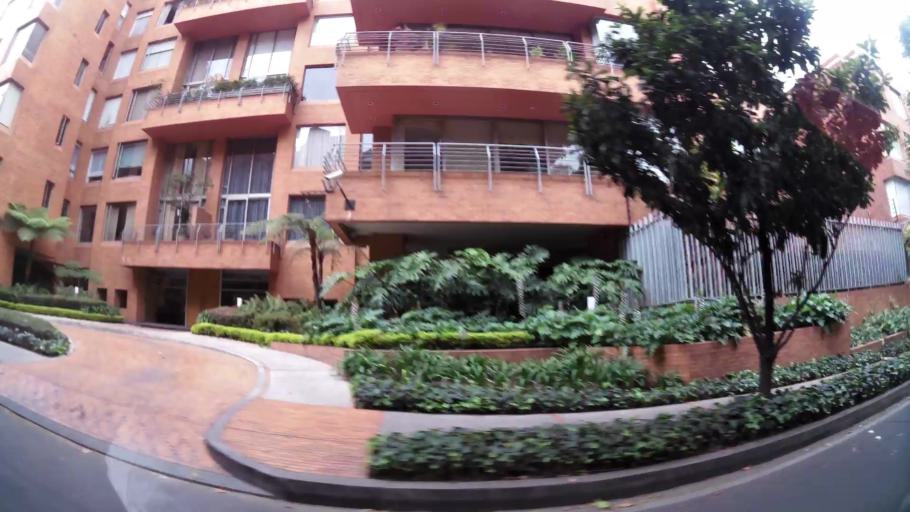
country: CO
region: Bogota D.C.
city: Barrio San Luis
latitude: 4.6709
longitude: -74.0462
